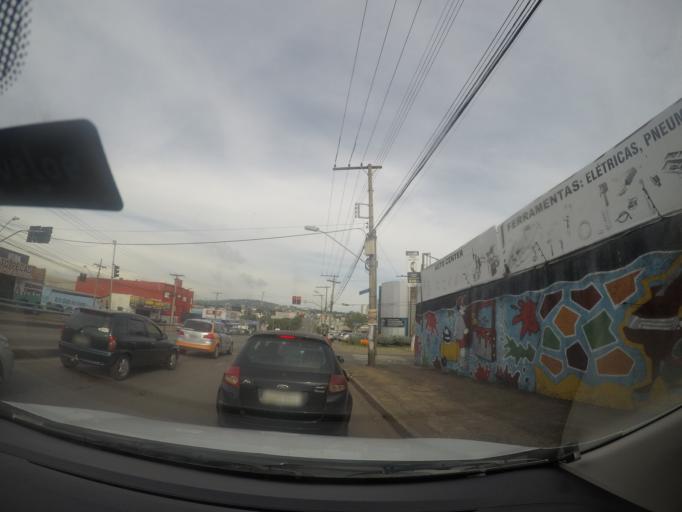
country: BR
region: Goias
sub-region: Goiania
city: Goiania
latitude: -16.6663
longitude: -49.3122
